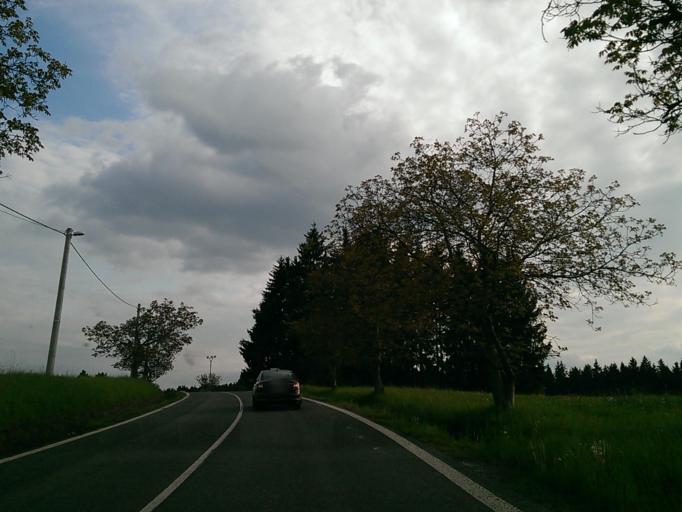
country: CZ
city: Plavy
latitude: 50.6861
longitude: 15.2990
